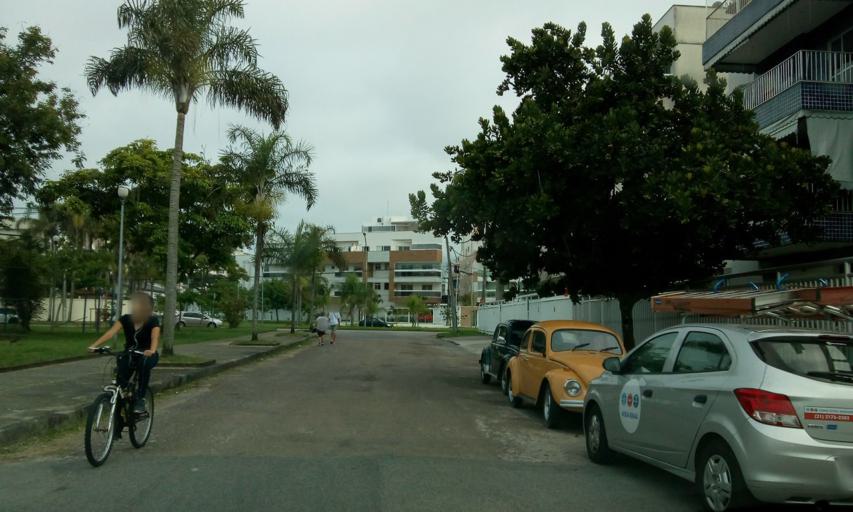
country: BR
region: Rio de Janeiro
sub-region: Nilopolis
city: Nilopolis
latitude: -23.0127
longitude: -43.4504
